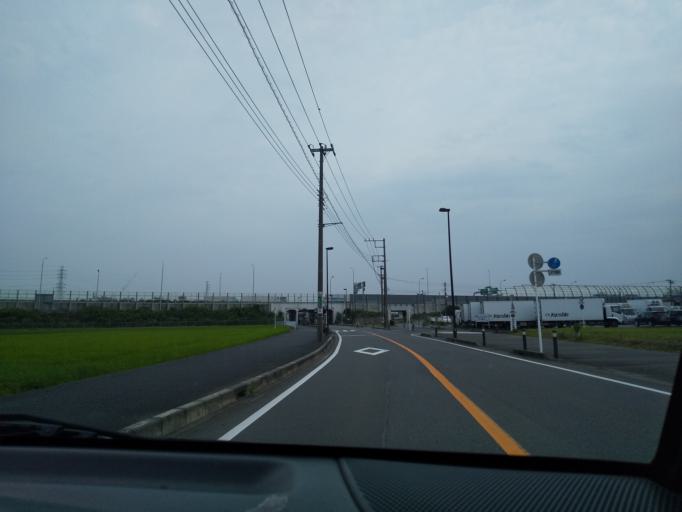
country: JP
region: Kanagawa
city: Atsugi
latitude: 35.4269
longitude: 139.3907
